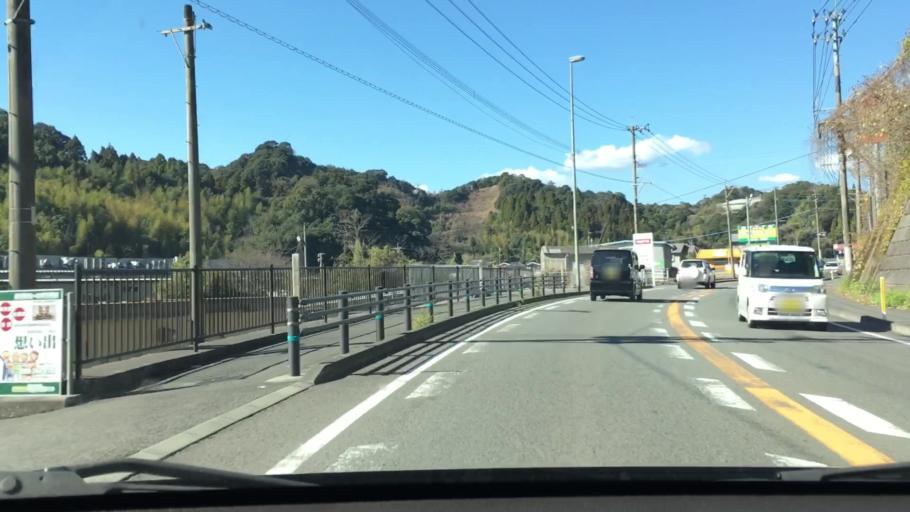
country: JP
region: Kagoshima
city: Kagoshima-shi
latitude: 31.6350
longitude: 130.5210
